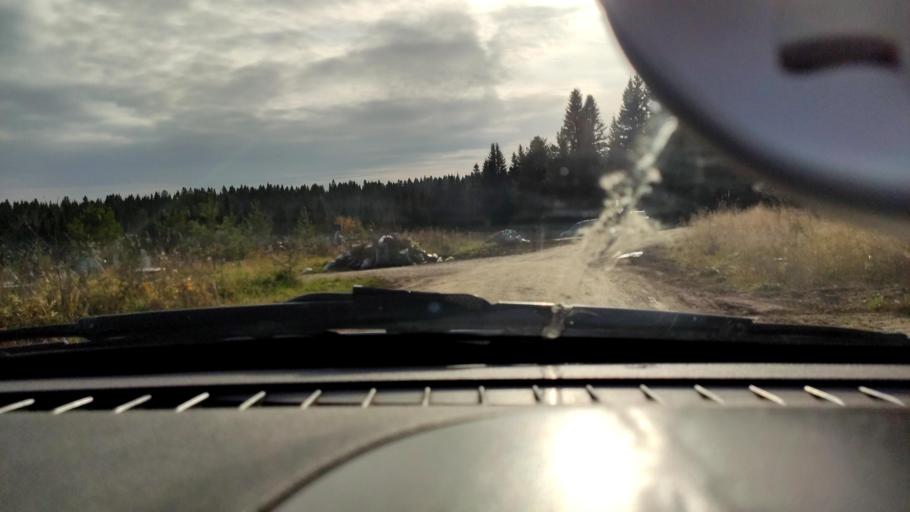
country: RU
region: Perm
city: Kultayevo
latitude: 57.8569
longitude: 55.8691
